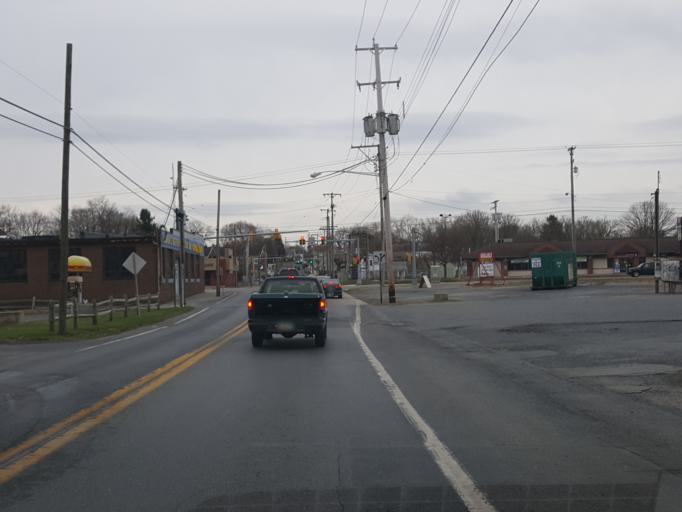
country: US
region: Pennsylvania
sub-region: Lebanon County
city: Pleasant Hill
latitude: 40.3393
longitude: -76.4398
